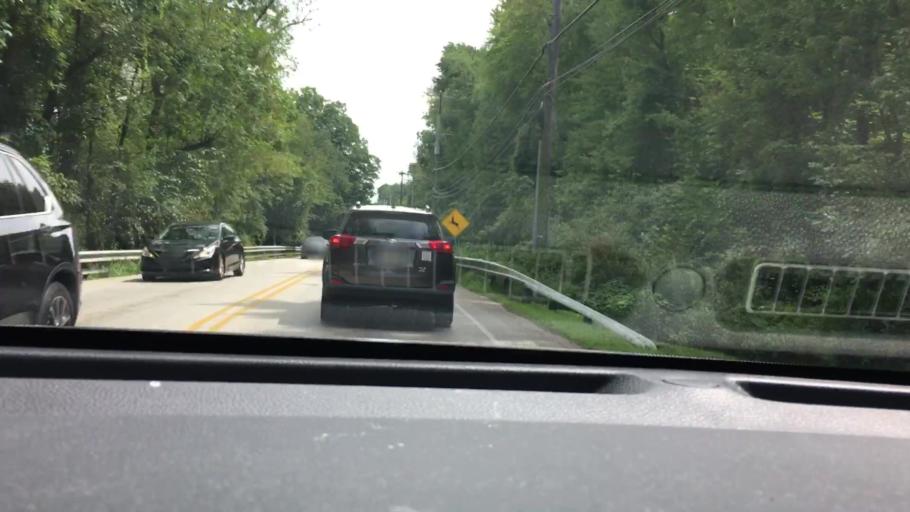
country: US
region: Pennsylvania
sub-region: Bucks County
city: Warminster Heights
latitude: 40.1599
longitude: -75.0765
